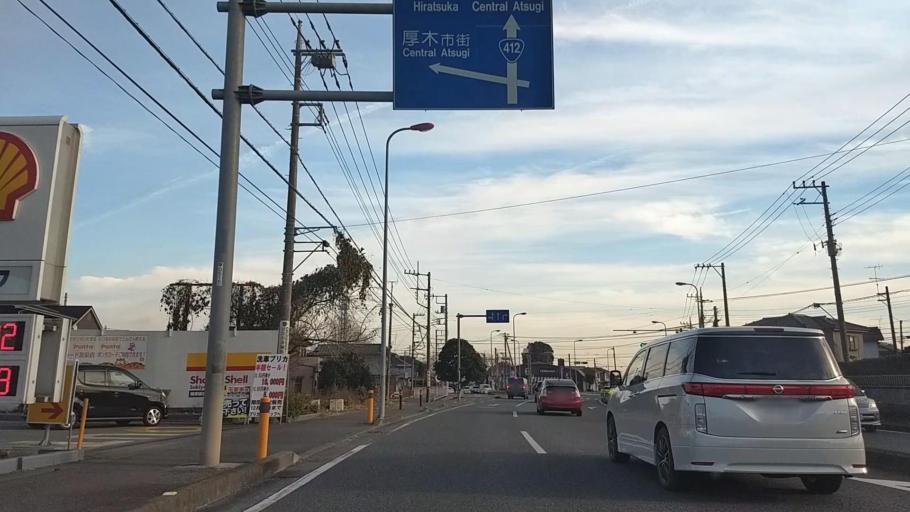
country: JP
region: Kanagawa
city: Atsugi
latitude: 35.4855
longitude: 139.3284
